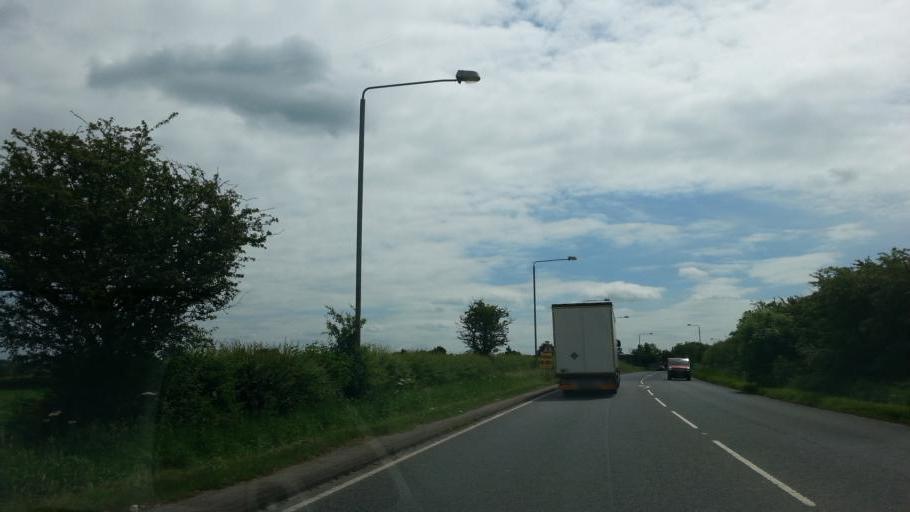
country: GB
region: England
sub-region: Nottinghamshire
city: Cotgrave
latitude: 52.8944
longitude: -1.0871
